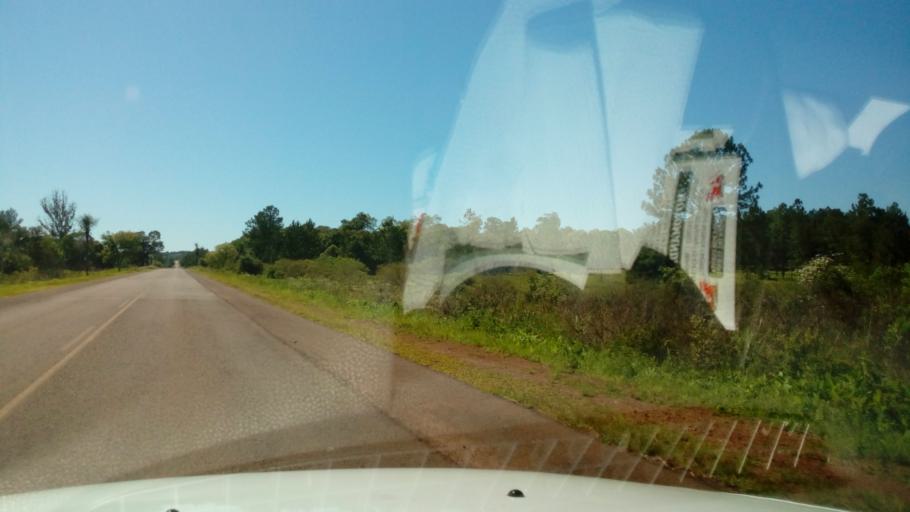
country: AR
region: Misiones
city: Almafuerte
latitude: -27.5709
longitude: -55.3925
